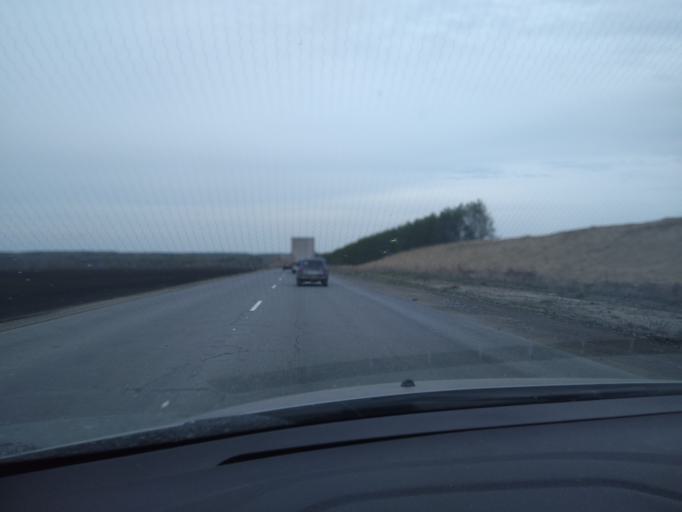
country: RU
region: Sverdlovsk
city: Kamyshlov
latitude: 56.8671
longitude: 62.9234
